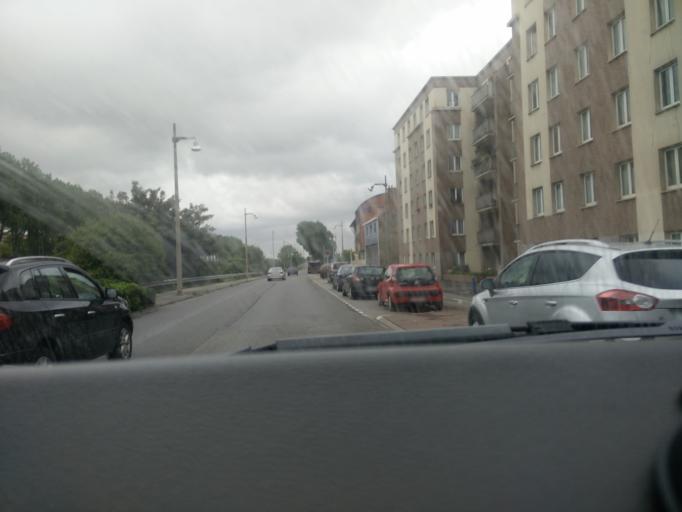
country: FR
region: Nord-Pas-de-Calais
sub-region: Departement du Nord
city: Dunkerque
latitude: 51.0283
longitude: 2.3722
